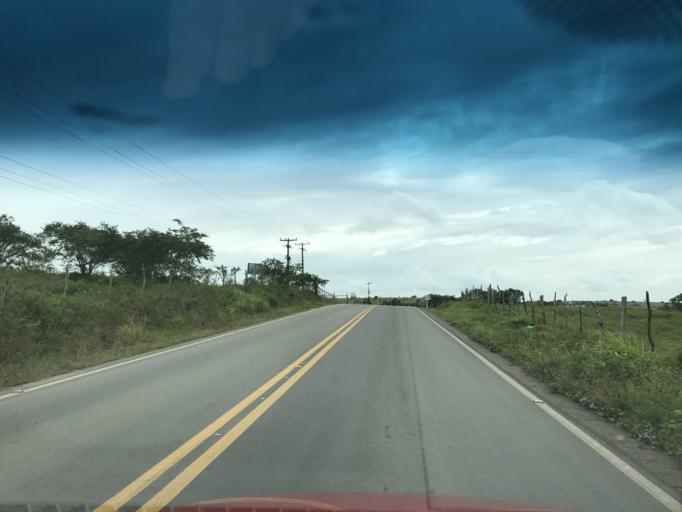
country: BR
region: Bahia
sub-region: Castro Alves
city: Castro Alves
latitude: -12.7581
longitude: -39.4172
